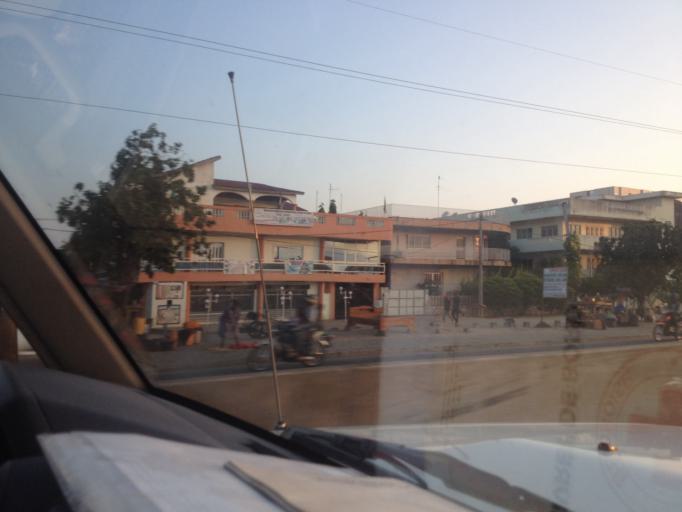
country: BJ
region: Littoral
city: Cotonou
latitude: 6.3691
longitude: 2.4867
